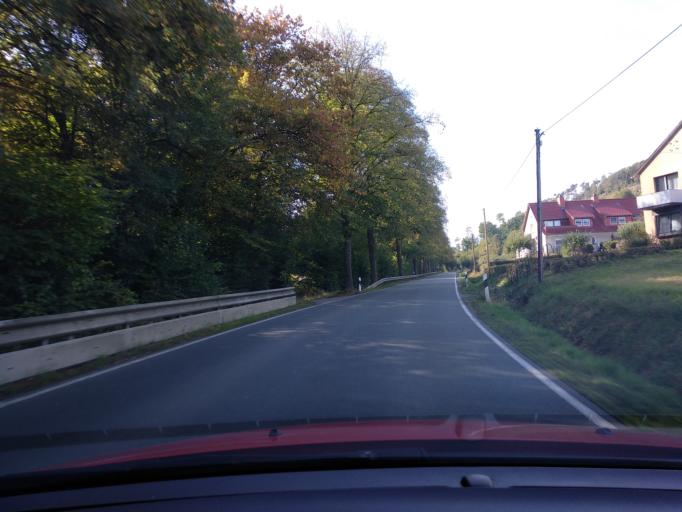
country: DE
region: North Rhine-Westphalia
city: Beverungen
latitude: 51.6717
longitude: 9.3646
